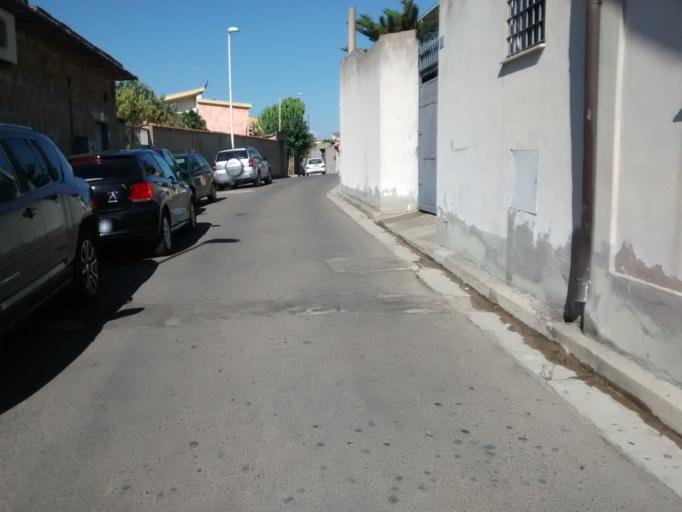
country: IT
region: Sardinia
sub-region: Provincia di Cagliari
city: Soleminis
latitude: 39.3465
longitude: 9.1805
